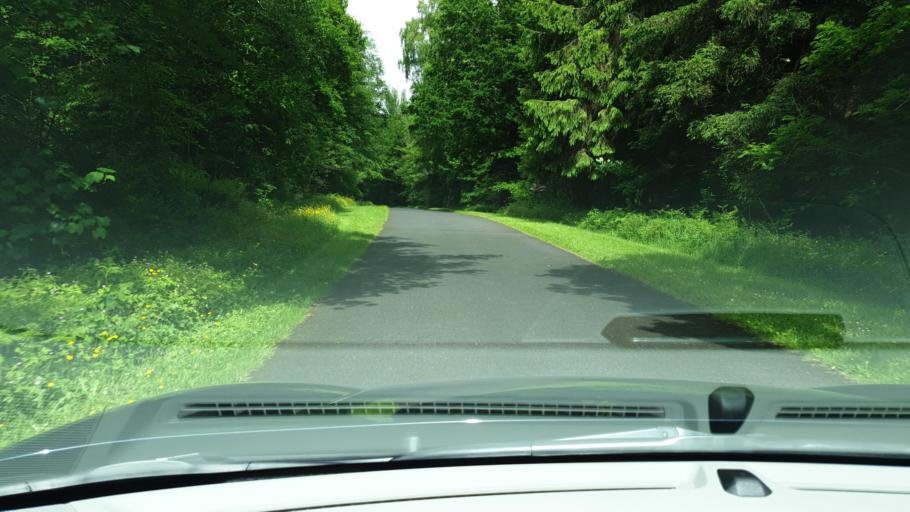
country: IE
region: Ulster
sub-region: An Cabhan
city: Kingscourt
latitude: 53.9162
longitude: -6.7888
